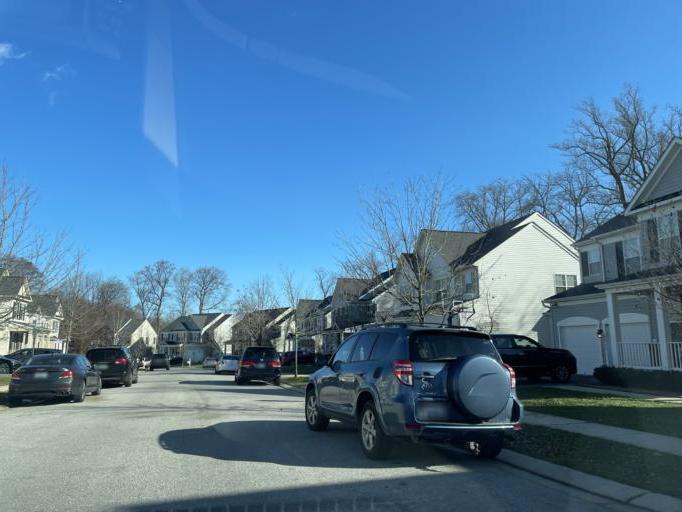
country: US
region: Maryland
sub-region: Baltimore County
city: Pikesville
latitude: 39.3703
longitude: -76.6700
